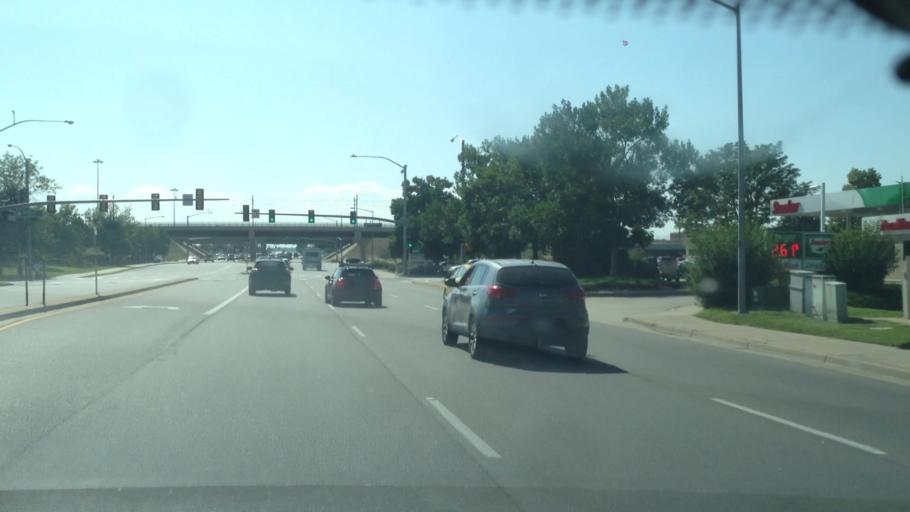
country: US
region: Colorado
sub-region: Adams County
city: Aurora
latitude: 39.7257
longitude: -104.8204
